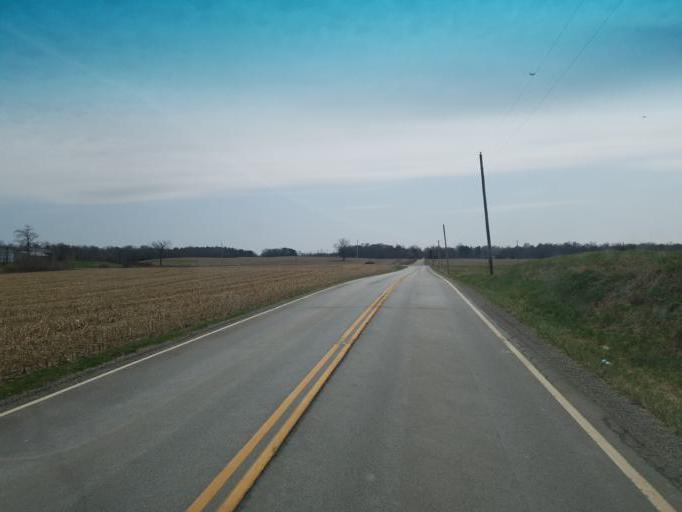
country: US
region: Ohio
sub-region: Crawford County
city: Galion
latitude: 40.7133
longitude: -82.7318
